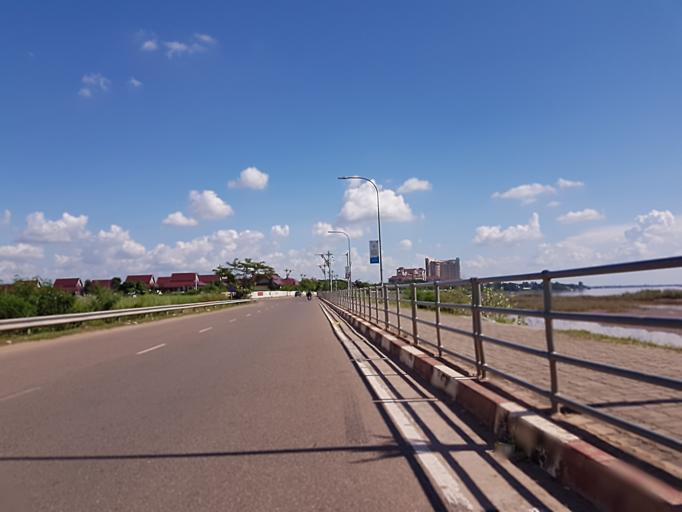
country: LA
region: Vientiane
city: Vientiane
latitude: 17.9532
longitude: 102.6137
